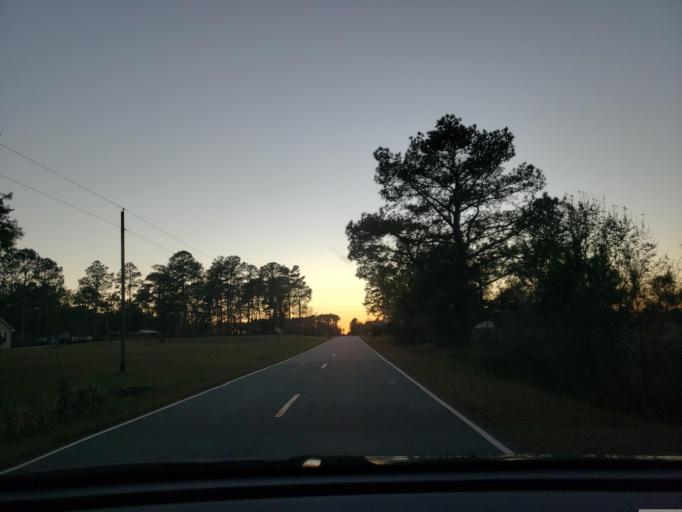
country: US
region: North Carolina
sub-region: Duplin County
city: Beulaville
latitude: 34.7569
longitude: -77.6886
